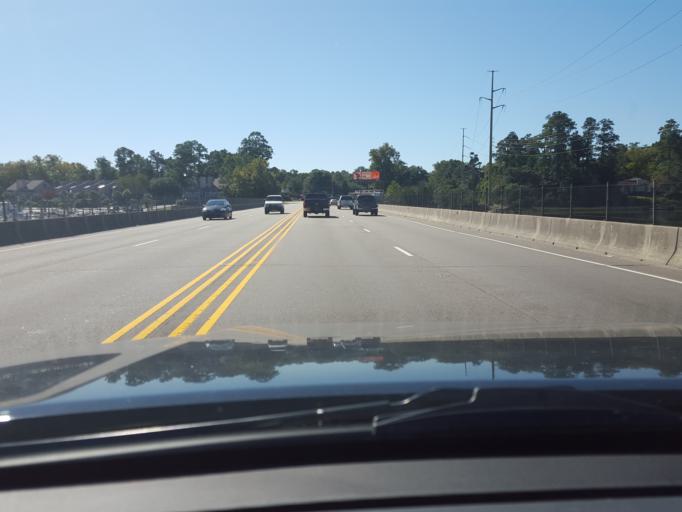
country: US
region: North Carolina
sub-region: New Hanover County
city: Seagate
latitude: 34.2163
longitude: -77.8339
